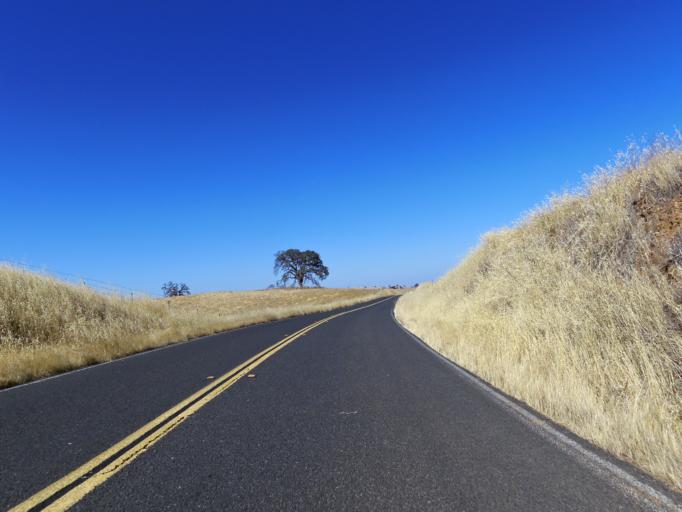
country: US
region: California
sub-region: Mariposa County
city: Mariposa
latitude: 37.4962
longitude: -120.1781
